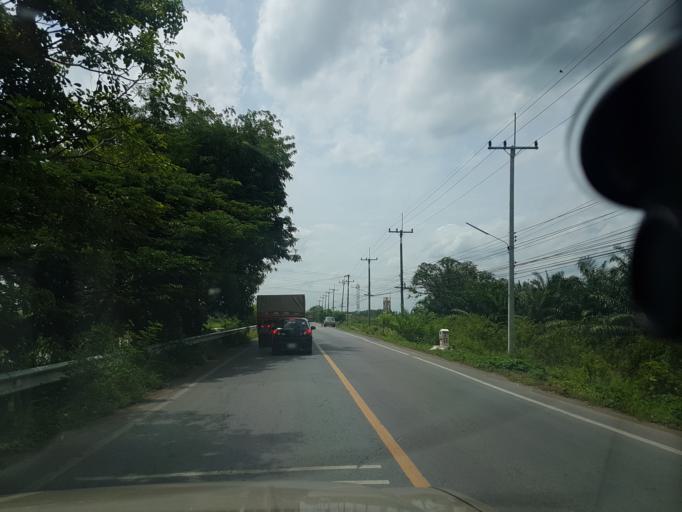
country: TH
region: Sara Buri
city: Nong Khae
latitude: 14.3101
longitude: 100.8863
